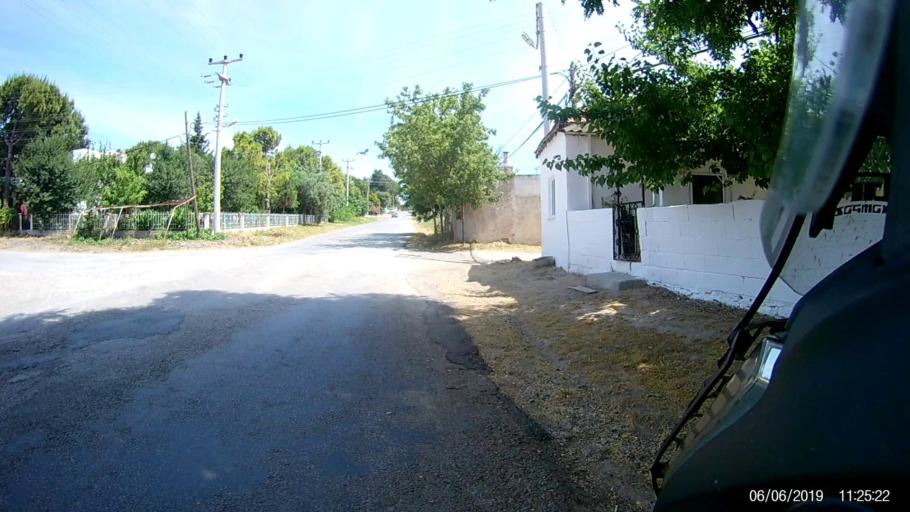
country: TR
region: Canakkale
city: Gulpinar
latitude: 39.6282
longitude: 26.1830
